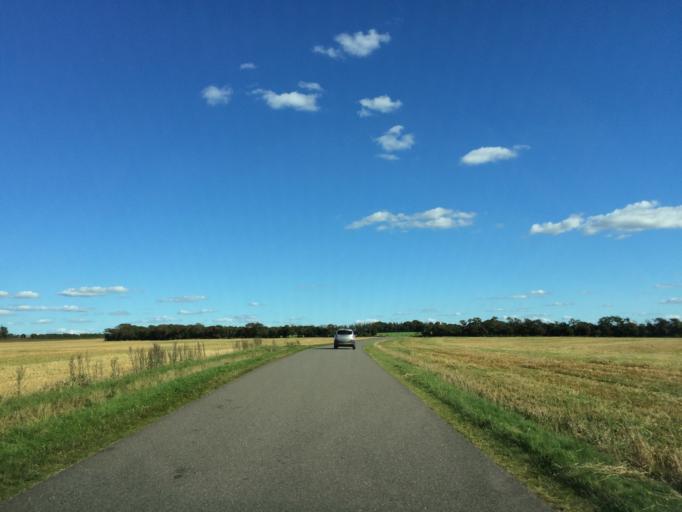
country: DK
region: Central Jutland
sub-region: Holstebro Kommune
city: Holstebro
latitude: 56.2658
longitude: 8.5321
